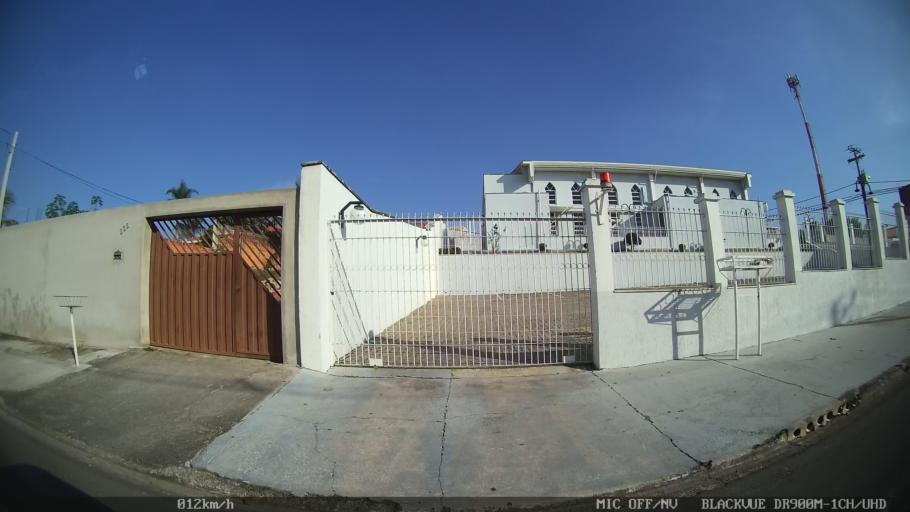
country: BR
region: Sao Paulo
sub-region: Campinas
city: Campinas
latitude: -22.9854
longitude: -47.1407
